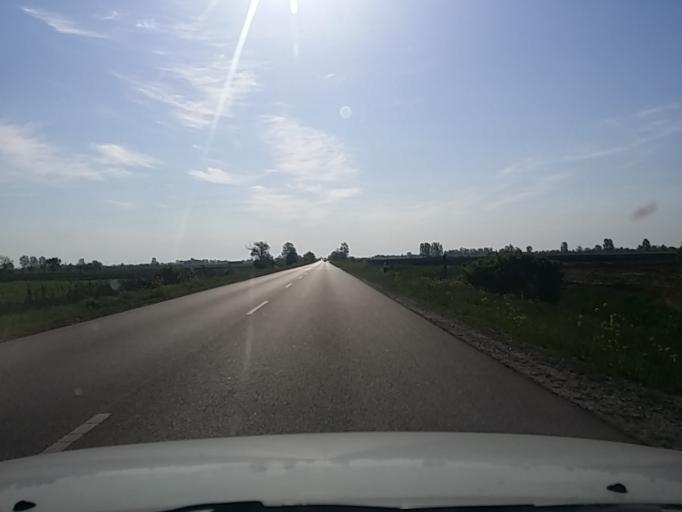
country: HU
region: Jasz-Nagykun-Szolnok
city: Mezotur
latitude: 46.9938
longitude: 20.6843
